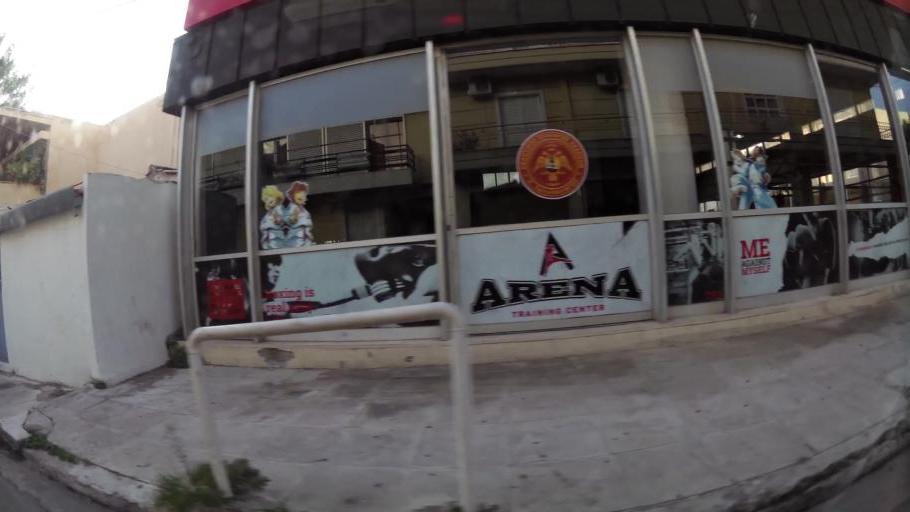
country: GR
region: Attica
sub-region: Nomarchia Anatolikis Attikis
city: Acharnes
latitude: 38.0844
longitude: 23.7346
